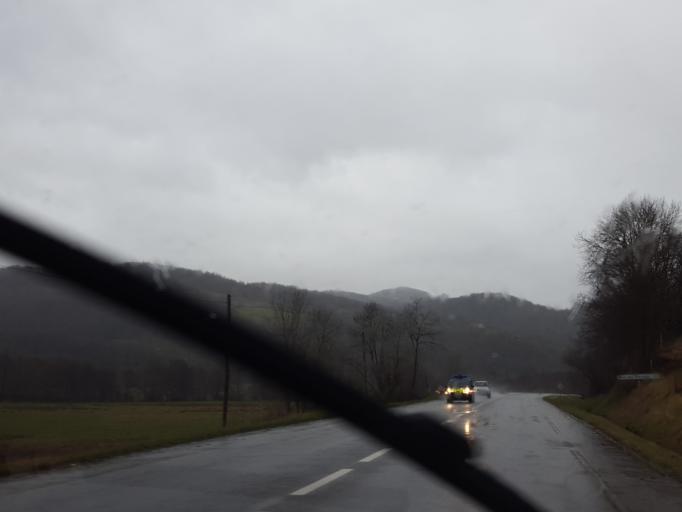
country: FR
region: Midi-Pyrenees
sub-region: Departement de l'Ariege
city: Montjoie-en-Couserans
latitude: 43.0130
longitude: 1.3684
